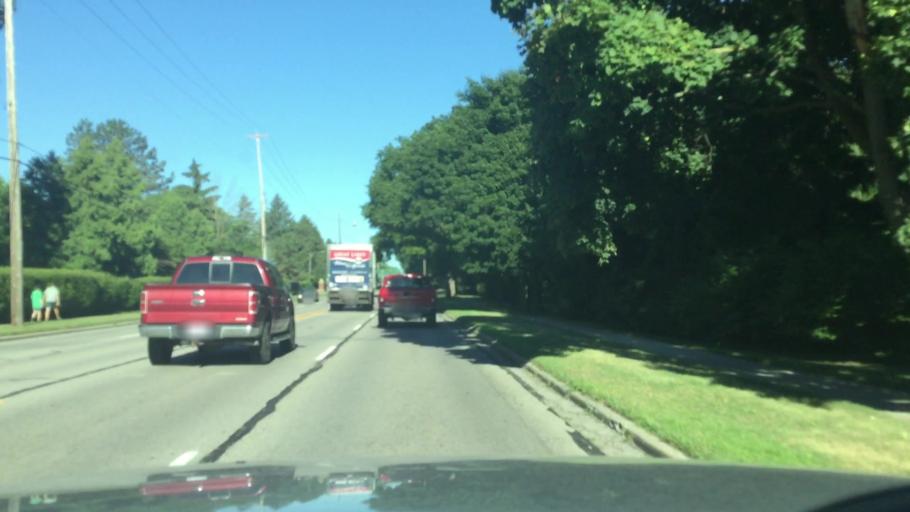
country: US
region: Michigan
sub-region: Saginaw County
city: Saginaw
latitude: 43.4152
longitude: -83.9984
